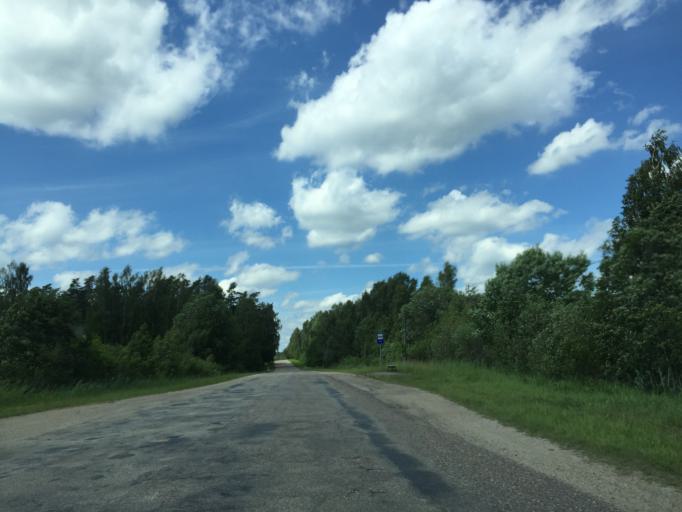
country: LV
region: Engure
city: Smarde
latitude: 56.9693
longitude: 23.3244
